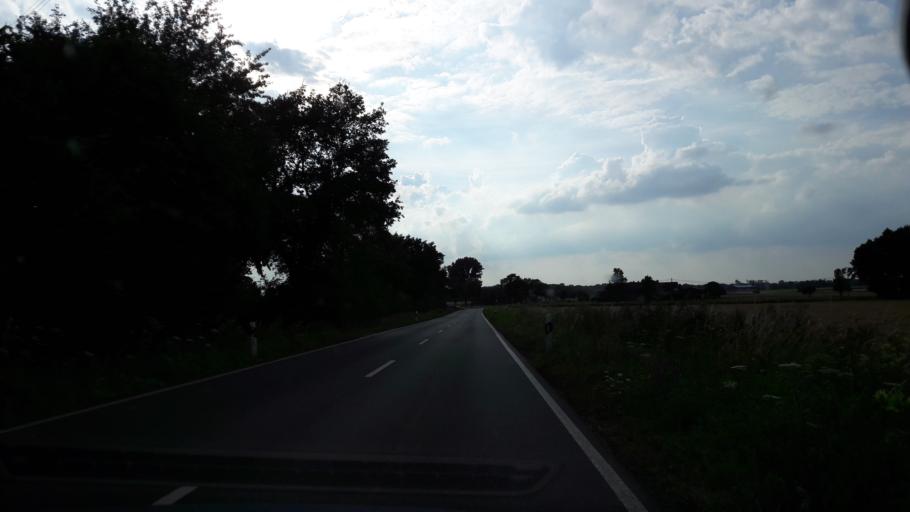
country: DE
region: North Rhine-Westphalia
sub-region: Regierungsbezirk Munster
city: Ennigerloh
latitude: 51.8130
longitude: 7.9760
